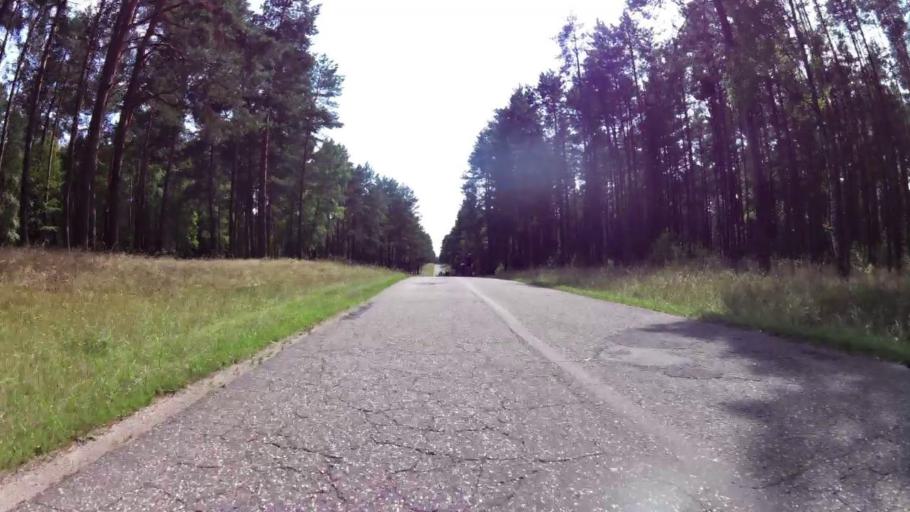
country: PL
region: West Pomeranian Voivodeship
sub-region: Powiat choszczenski
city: Drawno
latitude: 53.3270
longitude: 15.6926
